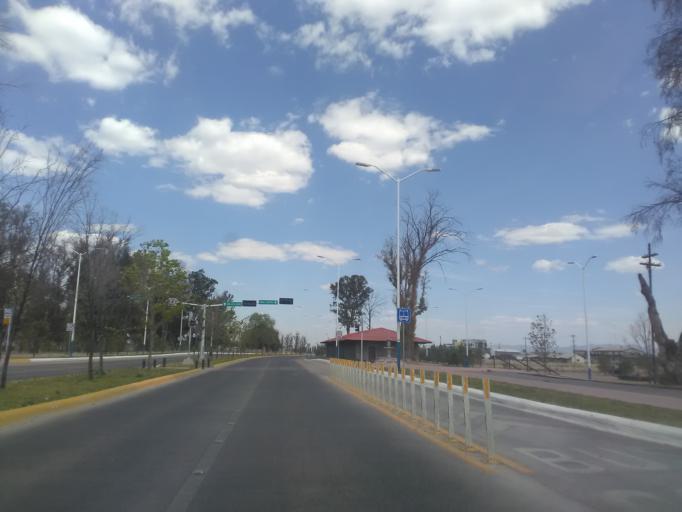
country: MX
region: Durango
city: Victoria de Durango
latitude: 24.0365
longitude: -104.6730
